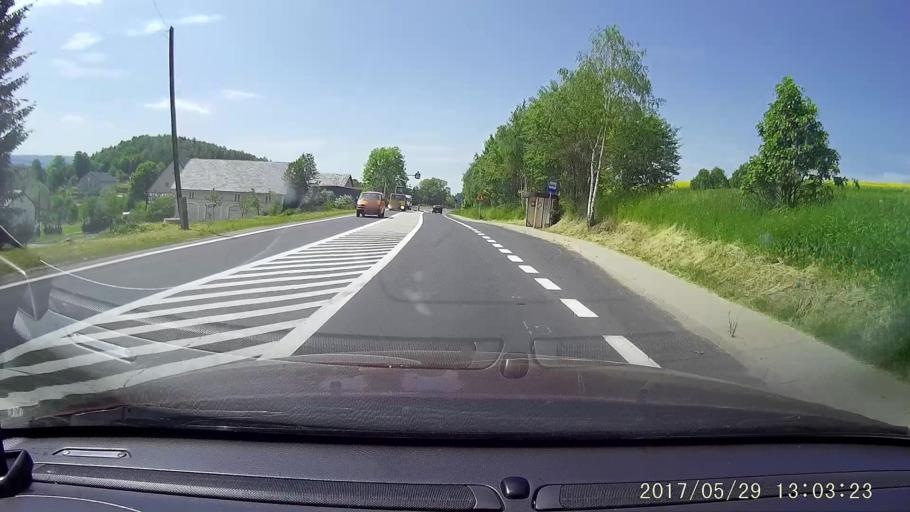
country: PL
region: Lower Silesian Voivodeship
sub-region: Powiat jeleniogorski
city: Stara Kamienica
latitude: 50.9230
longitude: 15.6139
